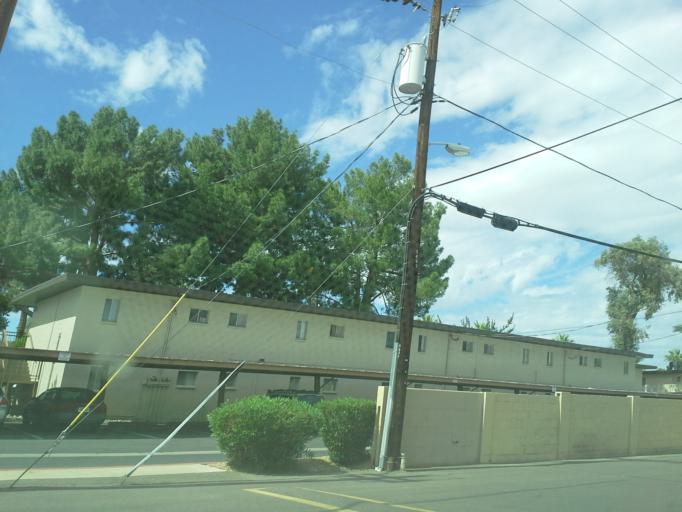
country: US
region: Arizona
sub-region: Maricopa County
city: Phoenix
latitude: 33.5097
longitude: -112.0861
